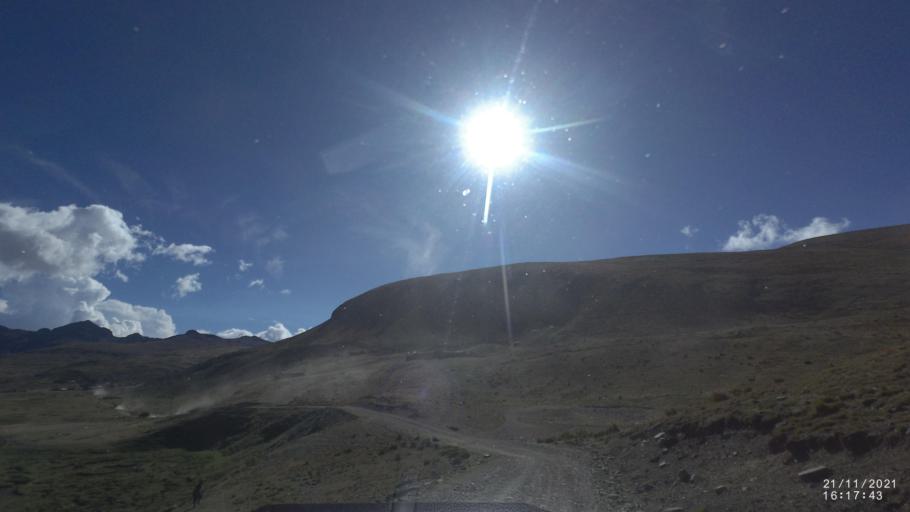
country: BO
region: Cochabamba
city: Cochabamba
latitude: -17.0041
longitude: -66.2817
